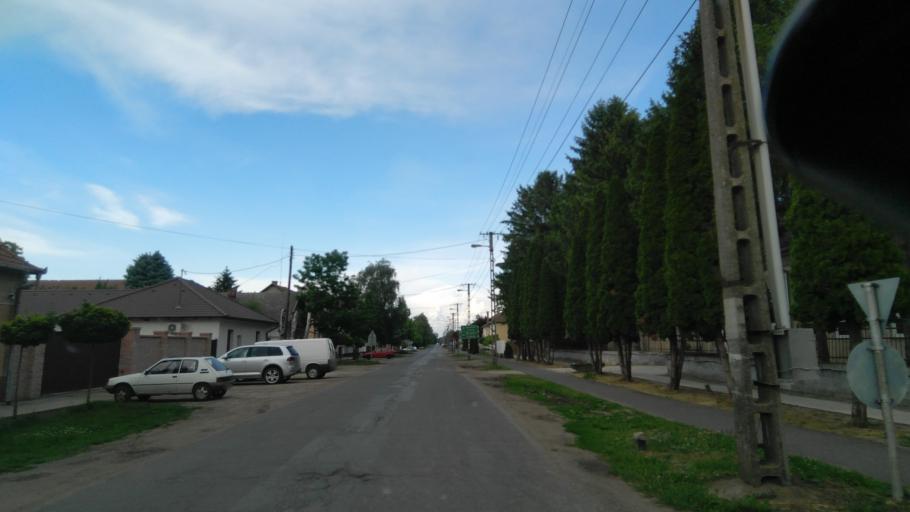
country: HU
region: Bekes
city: Kevermes
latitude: 46.4151
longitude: 21.1796
